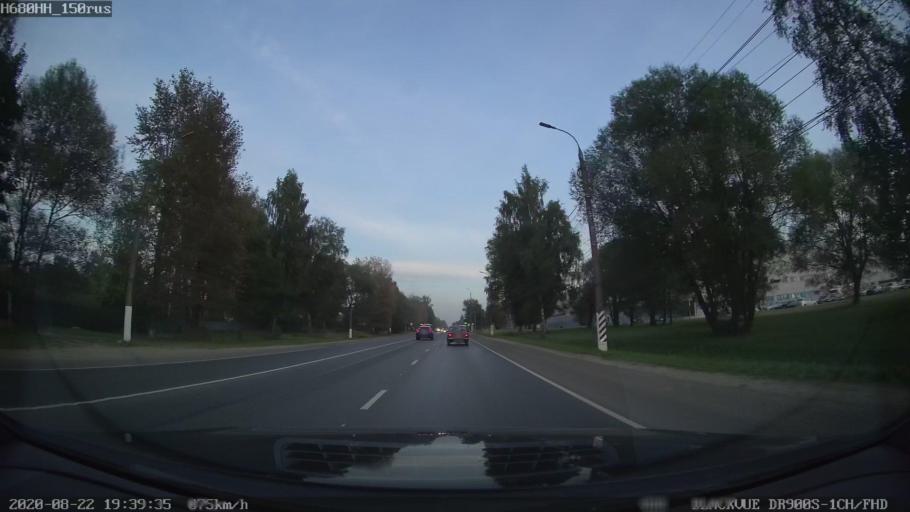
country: RU
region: Tverskaya
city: Sakharovo
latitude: 56.8070
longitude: 36.0159
